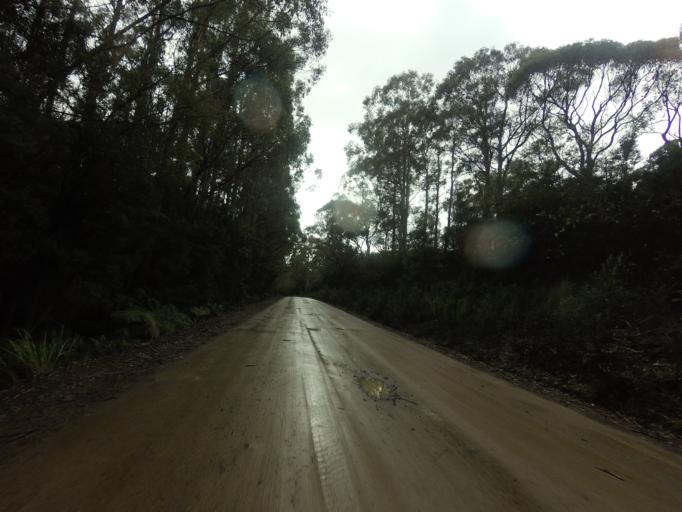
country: AU
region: Tasmania
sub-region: Huon Valley
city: Geeveston
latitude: -43.4578
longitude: 146.9020
